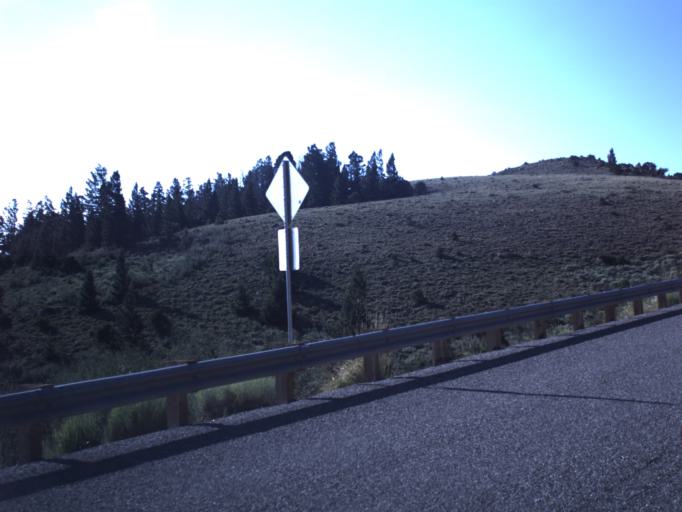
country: US
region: Utah
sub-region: Wayne County
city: Loa
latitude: 38.5992
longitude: -111.4676
